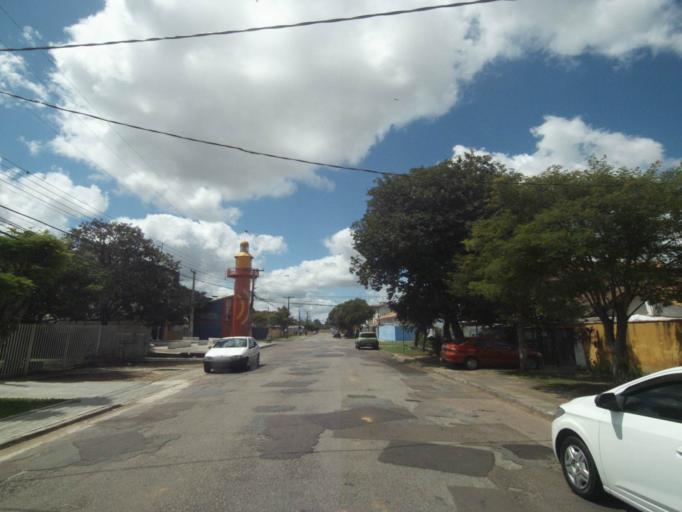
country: BR
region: Parana
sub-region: Pinhais
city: Pinhais
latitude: -25.4419
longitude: -49.2062
